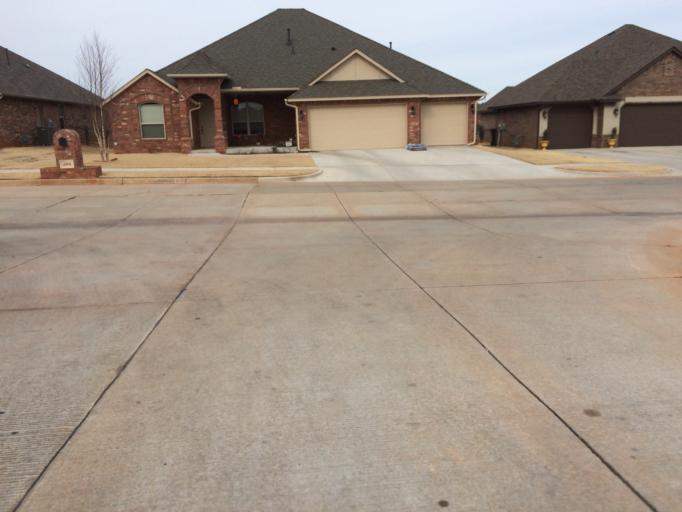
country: US
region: Oklahoma
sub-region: Cleveland County
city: Hall Park
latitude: 35.2160
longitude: -97.3897
